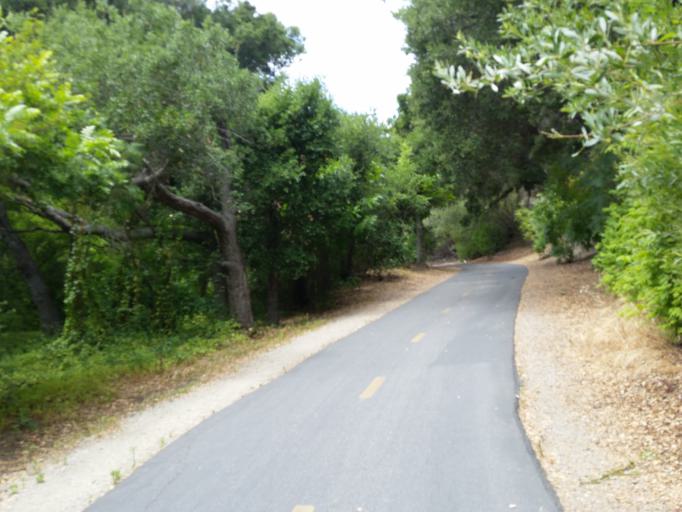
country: US
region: California
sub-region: San Luis Obispo County
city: Avila Beach
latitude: 35.1870
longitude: -120.7088
